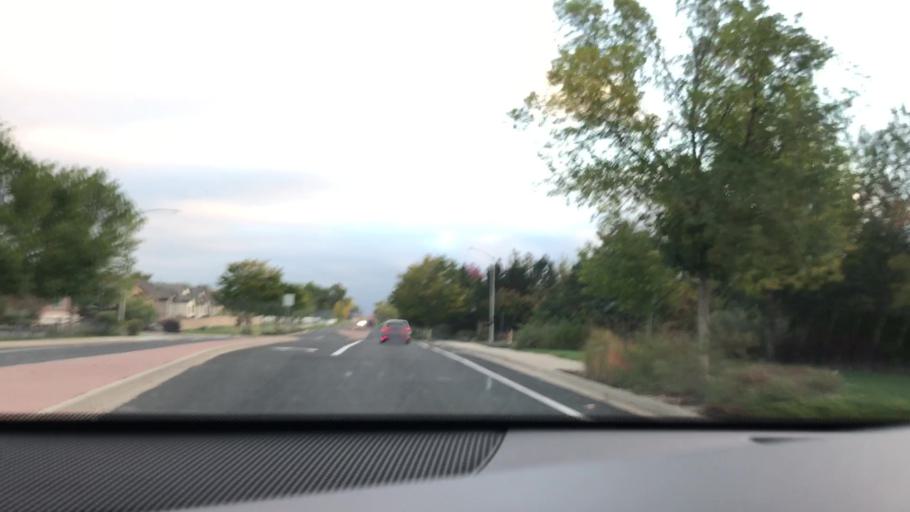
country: US
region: Colorado
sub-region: Broomfield County
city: Broomfield
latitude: 39.9482
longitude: -105.0624
